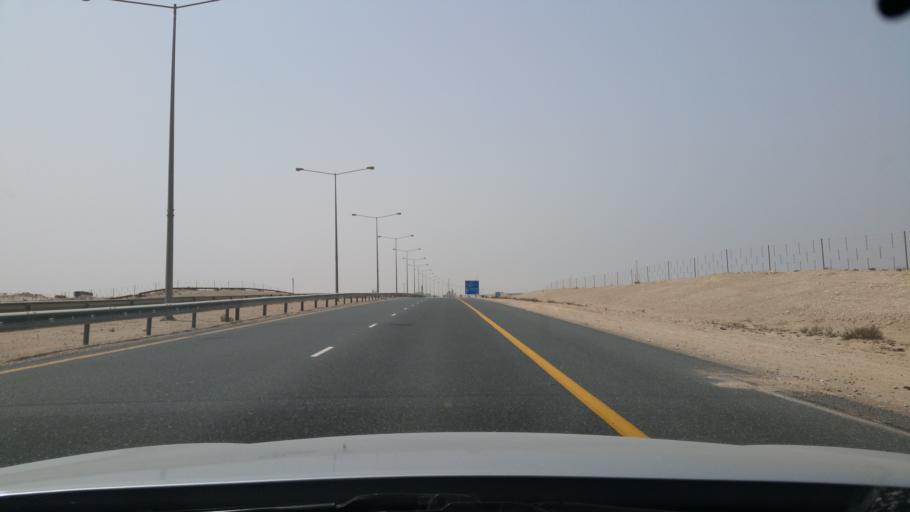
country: QA
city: Umm Bab
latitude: 25.3049
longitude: 50.7922
